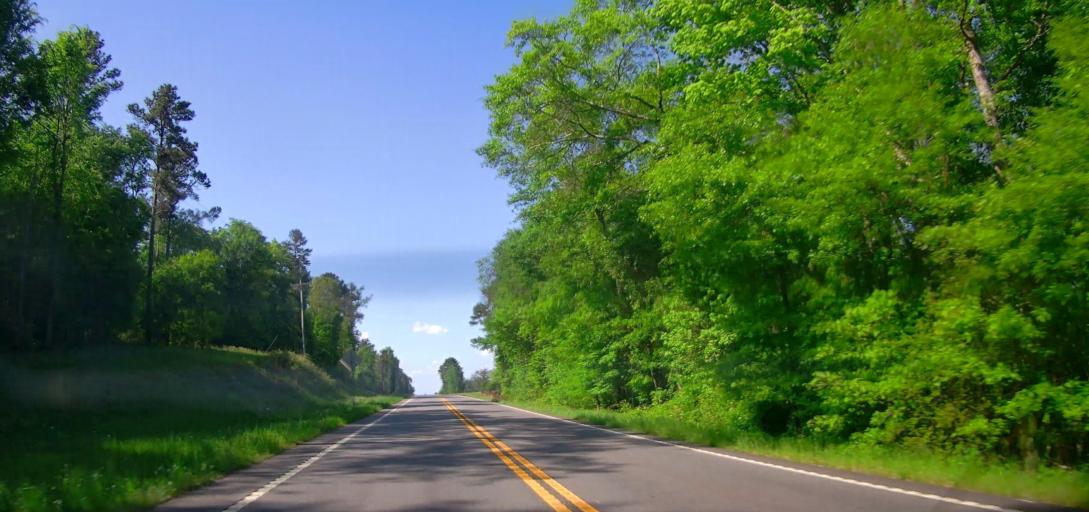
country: US
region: Georgia
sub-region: Morgan County
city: Madison
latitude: 33.6512
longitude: -83.4974
